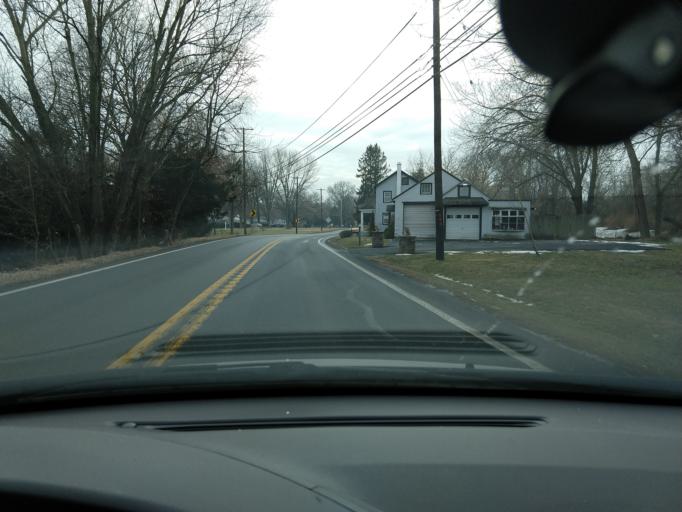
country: US
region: Pennsylvania
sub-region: Berks County
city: Amity Gardens
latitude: 40.2558
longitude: -75.7382
